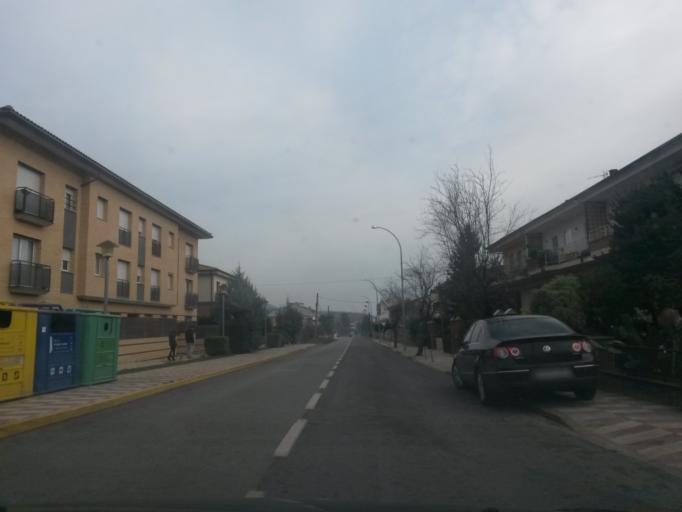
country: ES
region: Catalonia
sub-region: Provincia de Girona
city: Angles
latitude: 41.9564
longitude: 2.6290
